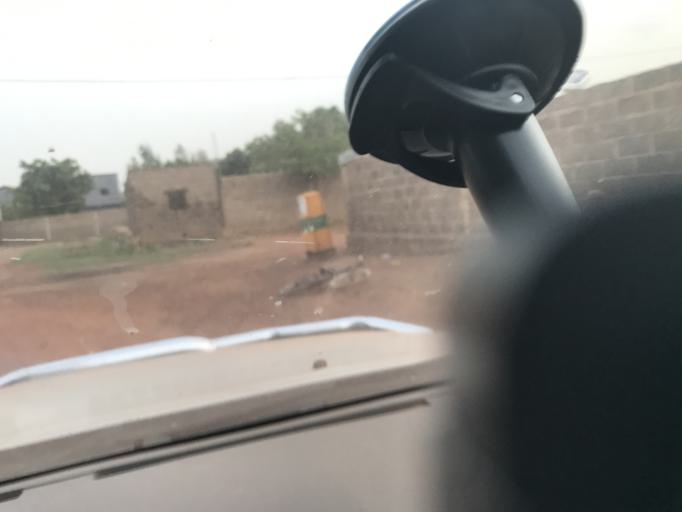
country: ML
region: Bamako
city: Bamako
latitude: 12.6523
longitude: -7.8838
